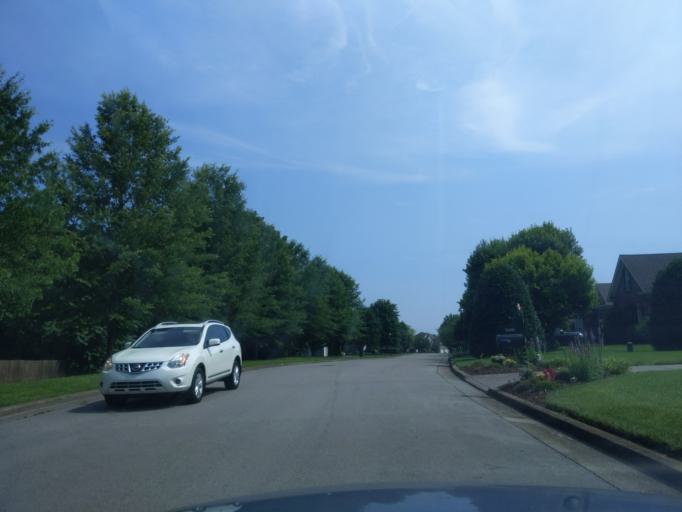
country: US
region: Tennessee
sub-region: Williamson County
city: Brentwood Estates
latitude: 36.0324
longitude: -86.7572
